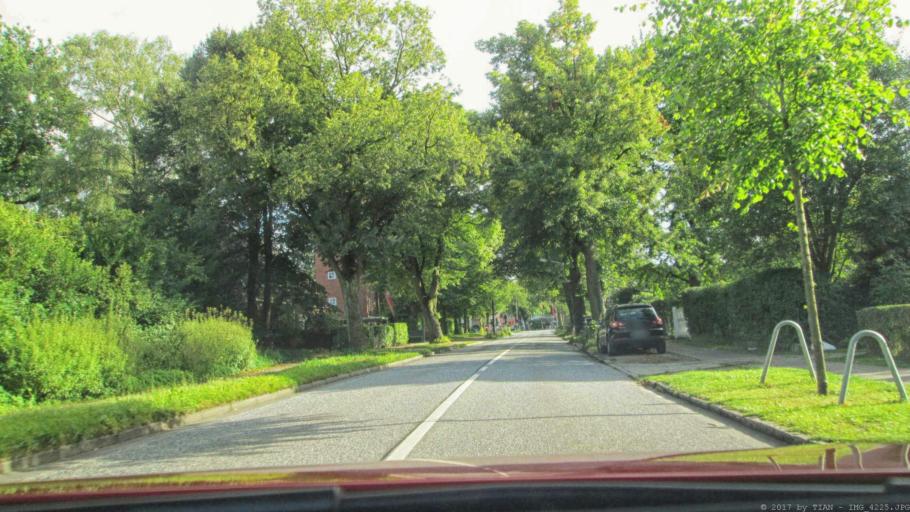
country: DE
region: Schleswig-Holstein
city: Halstenbek
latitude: 53.5782
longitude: 9.8233
